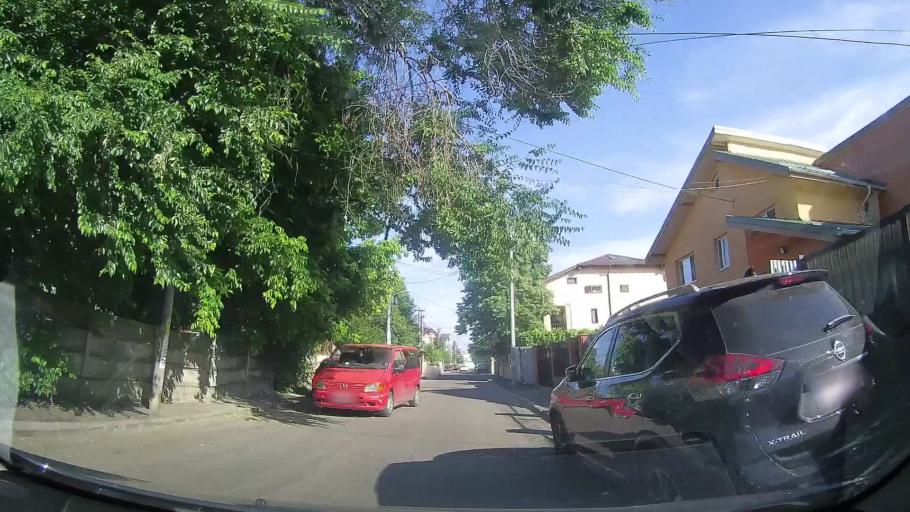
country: RO
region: Bucuresti
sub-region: Municipiul Bucuresti
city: Bucharest
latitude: 44.4095
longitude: 26.1333
